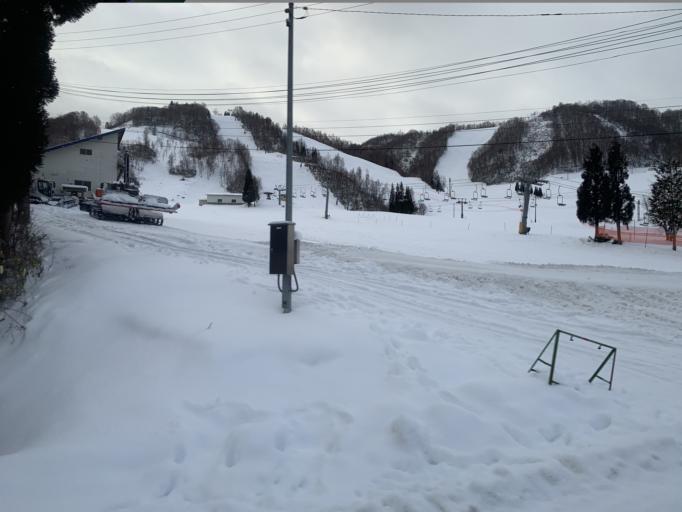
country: JP
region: Gifu
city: Takayama
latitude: 36.1755
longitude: 137.4931
